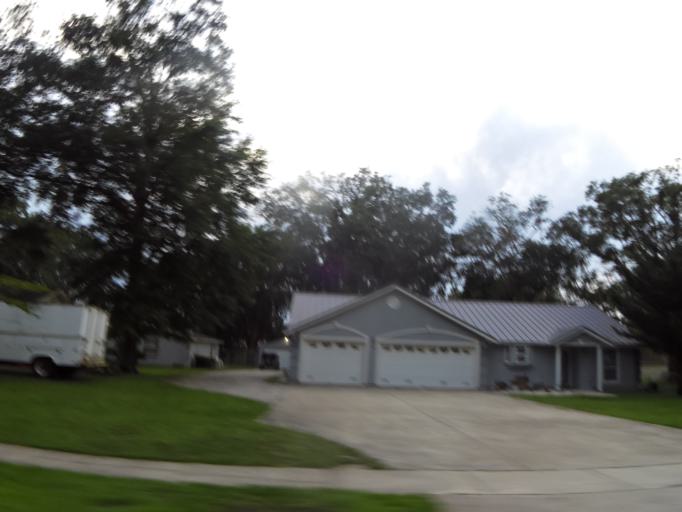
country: US
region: Florida
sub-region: Clay County
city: Bellair-Meadowbrook Terrace
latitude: 30.2904
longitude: -81.7982
